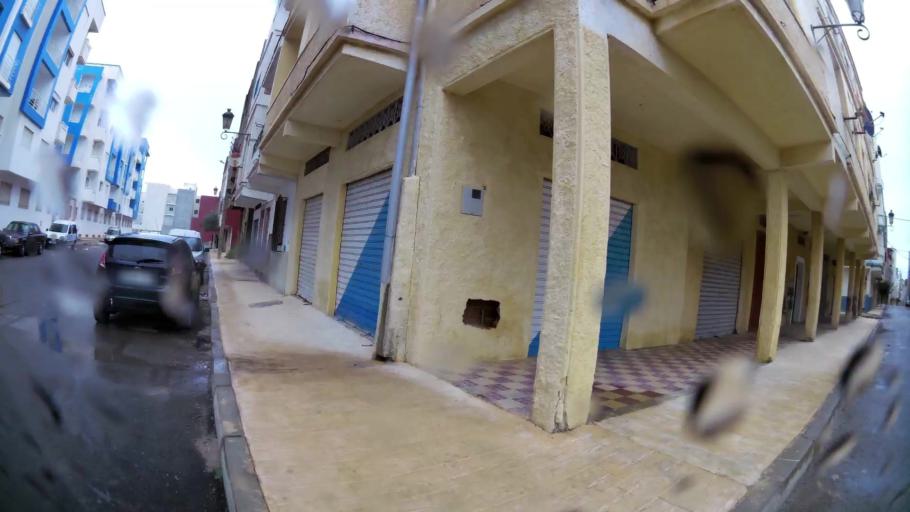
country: MA
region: Tanger-Tetouan
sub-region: Tetouan
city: Martil
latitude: 35.6147
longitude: -5.2857
